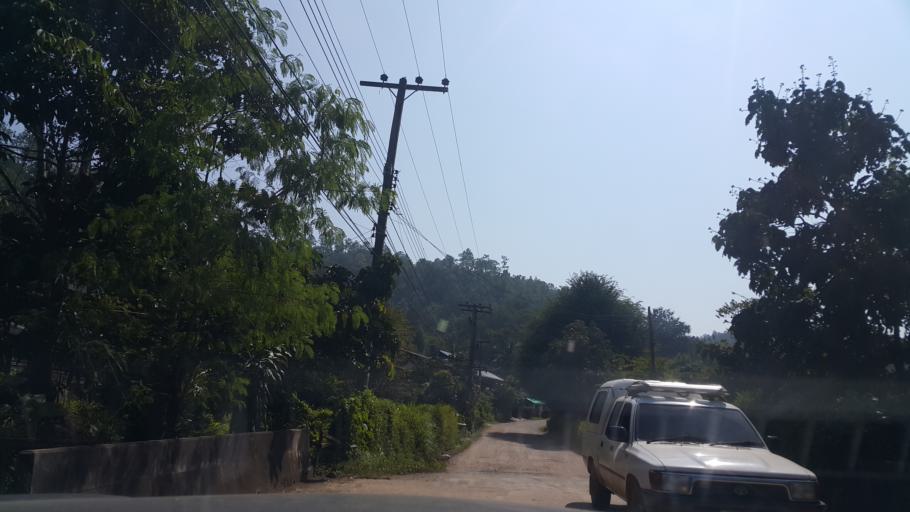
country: TH
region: Chiang Mai
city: Samoeng
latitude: 18.9113
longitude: 98.6039
